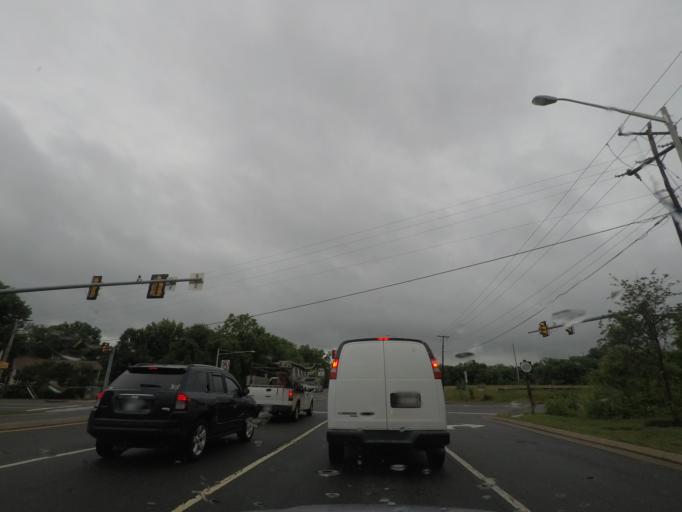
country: US
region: Virginia
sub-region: Loudoun County
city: Leesburg
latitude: 39.0991
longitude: -77.5771
